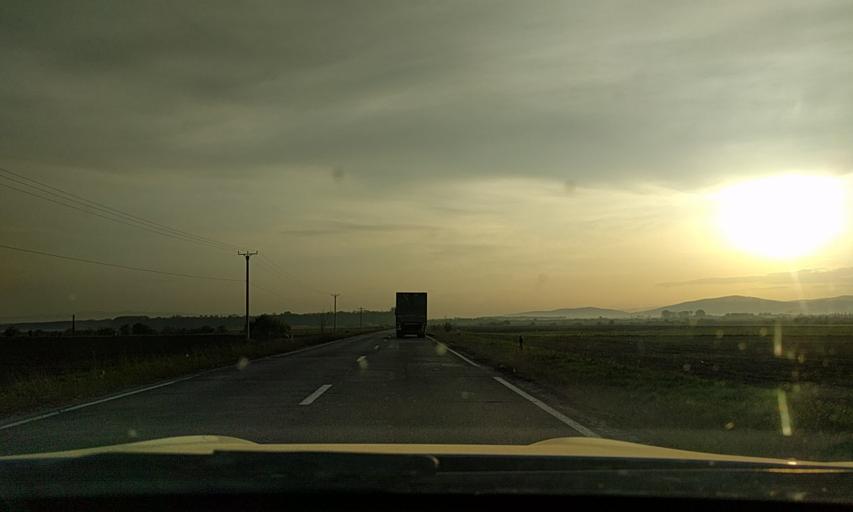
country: RO
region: Brasov
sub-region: Comuna Harman
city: Harman
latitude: 45.7215
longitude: 25.7236
